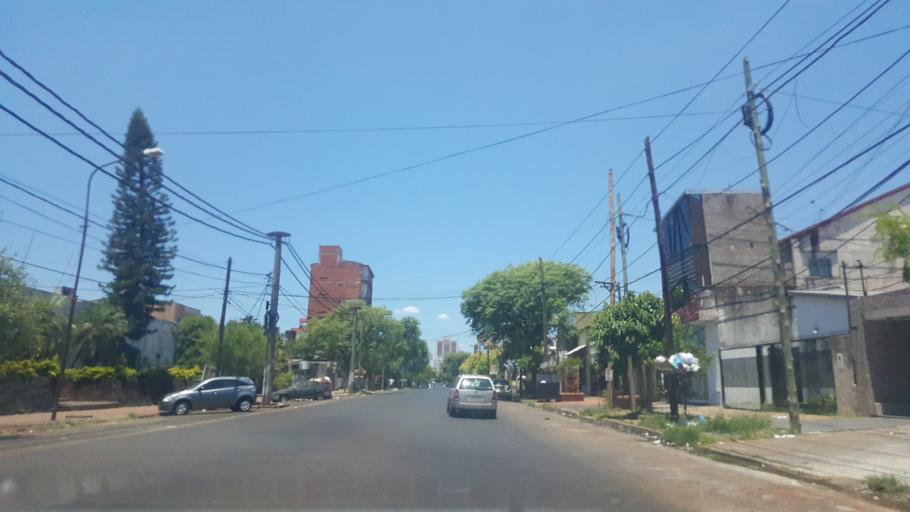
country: AR
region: Misiones
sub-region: Departamento de Capital
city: Posadas
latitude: -27.3664
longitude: -55.9084
